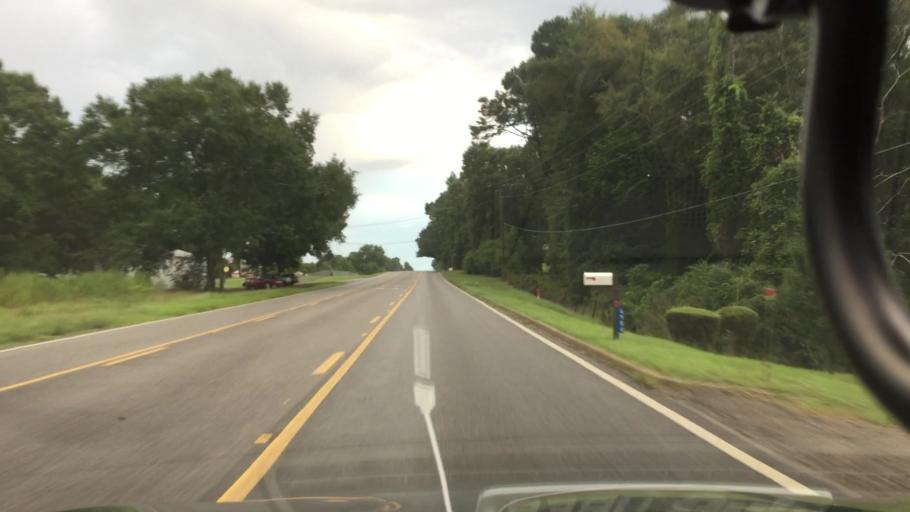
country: US
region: Alabama
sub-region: Pike County
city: Troy
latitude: 31.6854
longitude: -85.9594
